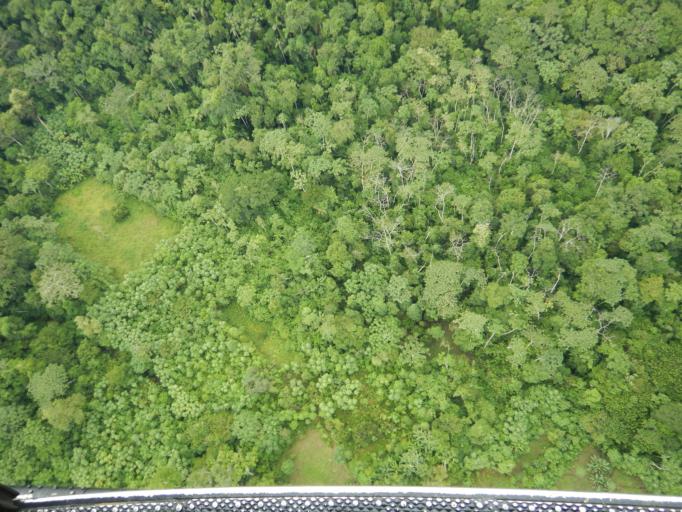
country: BO
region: Santa Cruz
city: Comarapa
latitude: -17.3458
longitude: -64.5183
